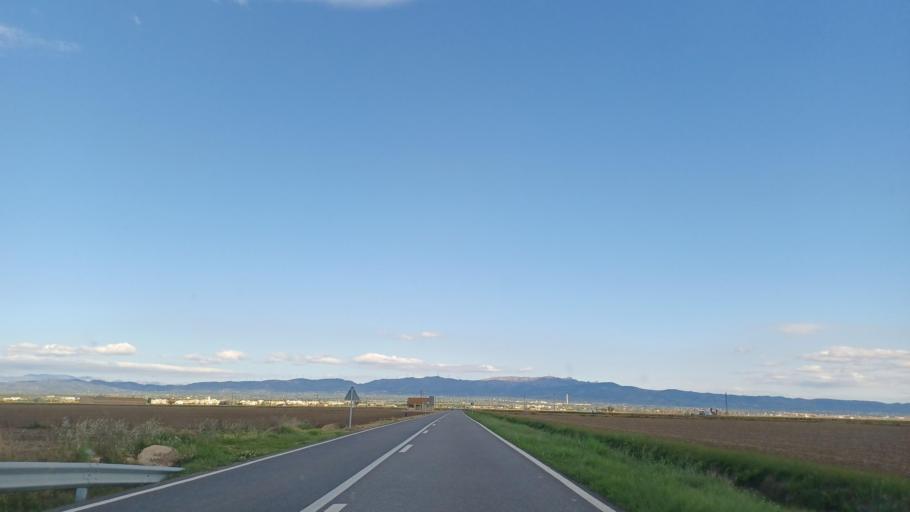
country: ES
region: Catalonia
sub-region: Provincia de Tarragona
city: Deltebre
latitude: 40.7551
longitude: 0.7027
